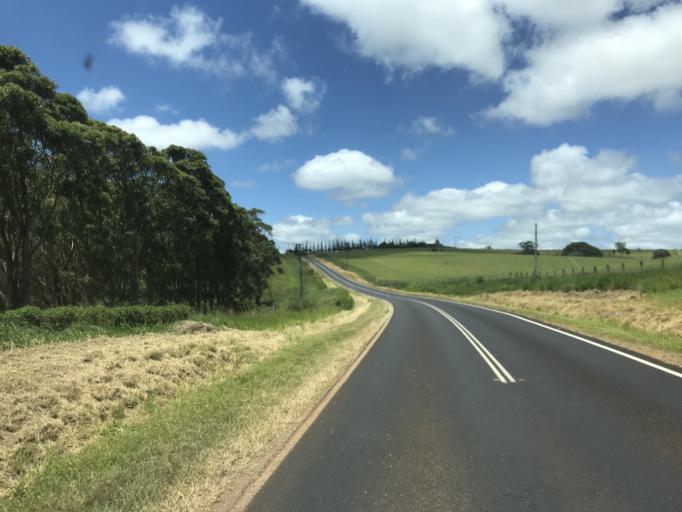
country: AU
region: Queensland
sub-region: Tablelands
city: Ravenshoe
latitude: -17.5063
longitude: 145.4759
